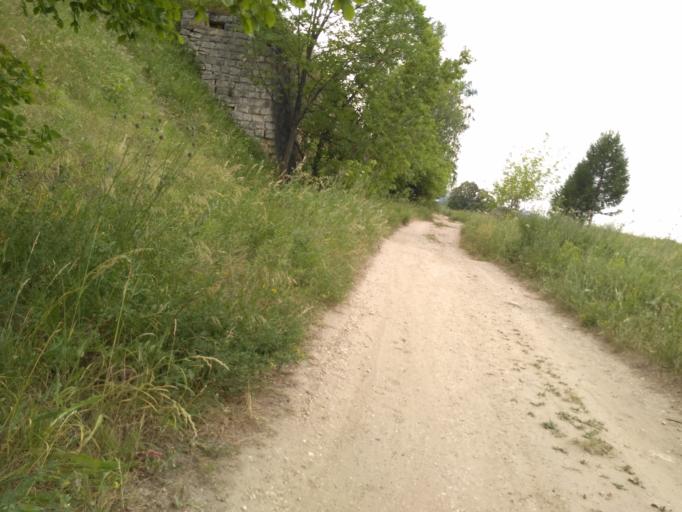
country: RU
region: Nizjnij Novgorod
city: Nizhniy Novgorod
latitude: 56.2687
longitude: 43.9723
